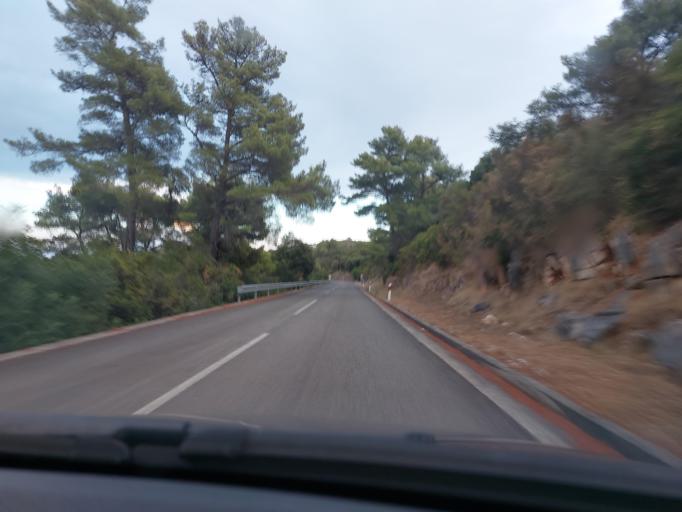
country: HR
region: Dubrovacko-Neretvanska
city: Smokvica
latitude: 42.7693
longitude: 16.8630
